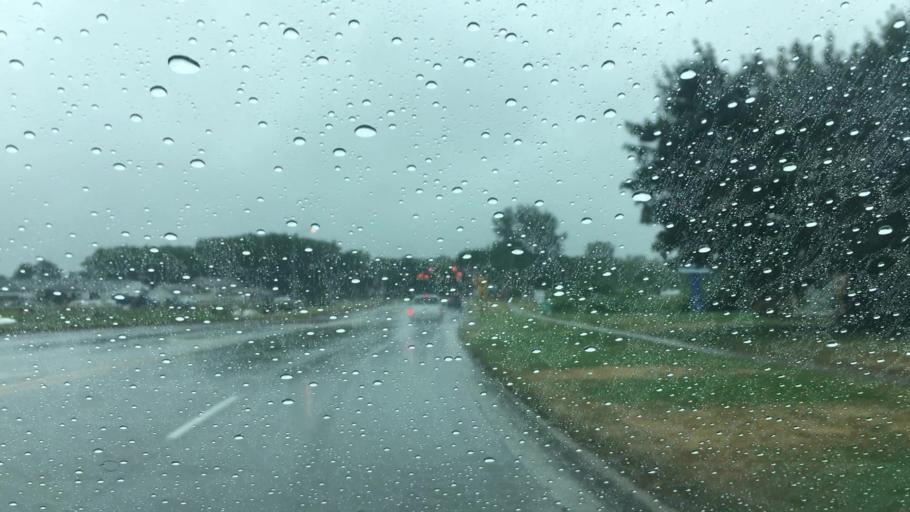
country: US
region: Michigan
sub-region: Ottawa County
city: Hudsonville
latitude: 42.8873
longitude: -85.8362
